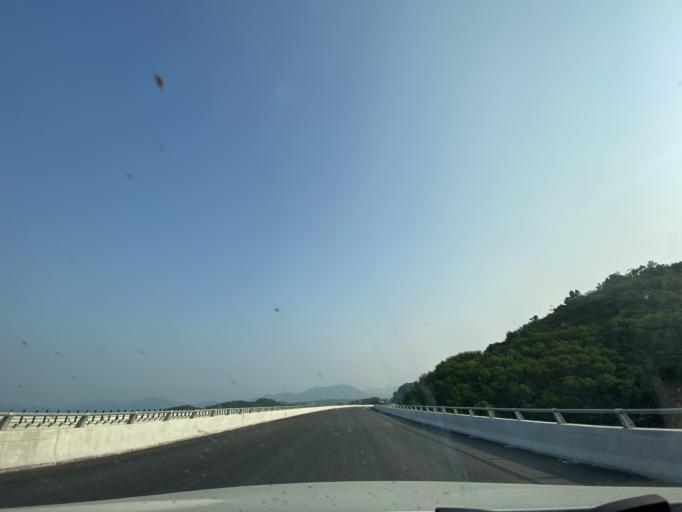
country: CN
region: Hainan
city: Xiangshui
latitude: 18.6609
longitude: 109.6288
